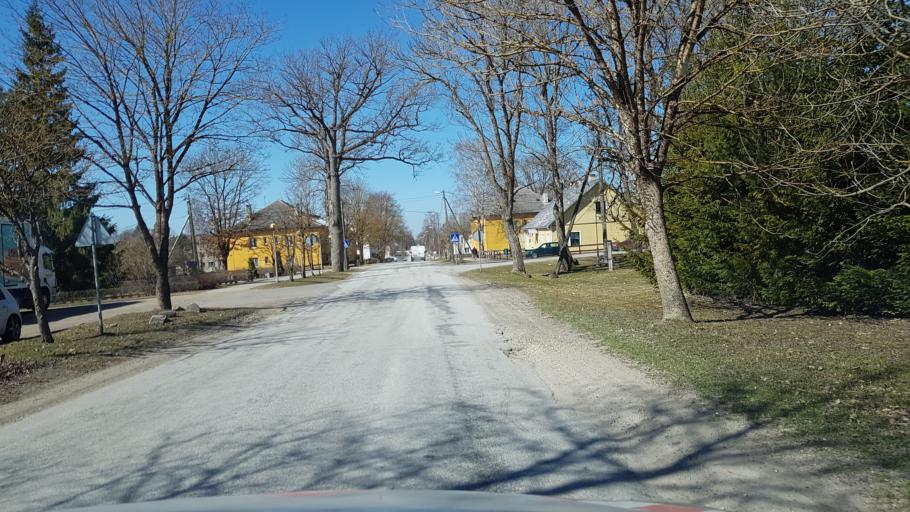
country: EE
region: Laeaene-Virumaa
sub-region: Rakke vald
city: Rakke
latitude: 58.9880
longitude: 26.2423
